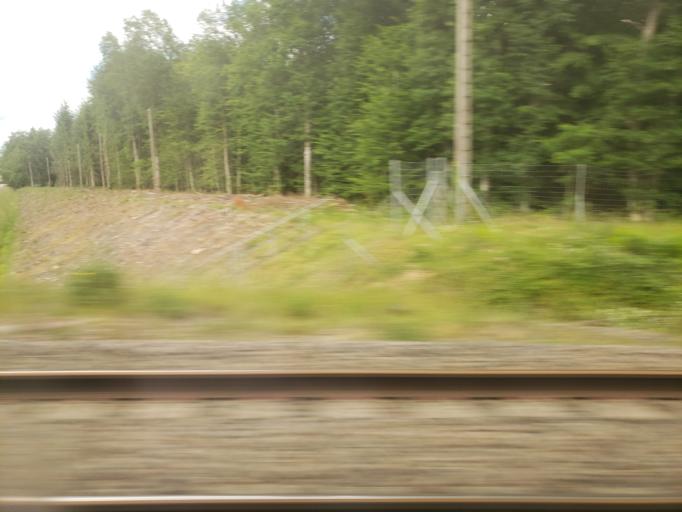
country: FR
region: Bourgogne
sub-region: Departement de la Cote-d'Or
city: Saulieu
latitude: 47.3546
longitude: 4.2427
